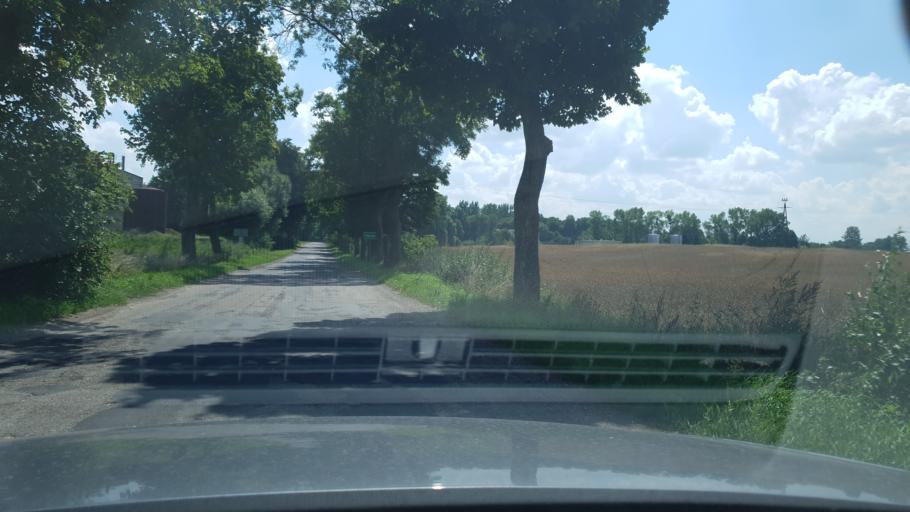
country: PL
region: Kujawsko-Pomorskie
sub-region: Powiat wabrzeski
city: Pluznica
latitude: 53.3508
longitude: 18.8291
